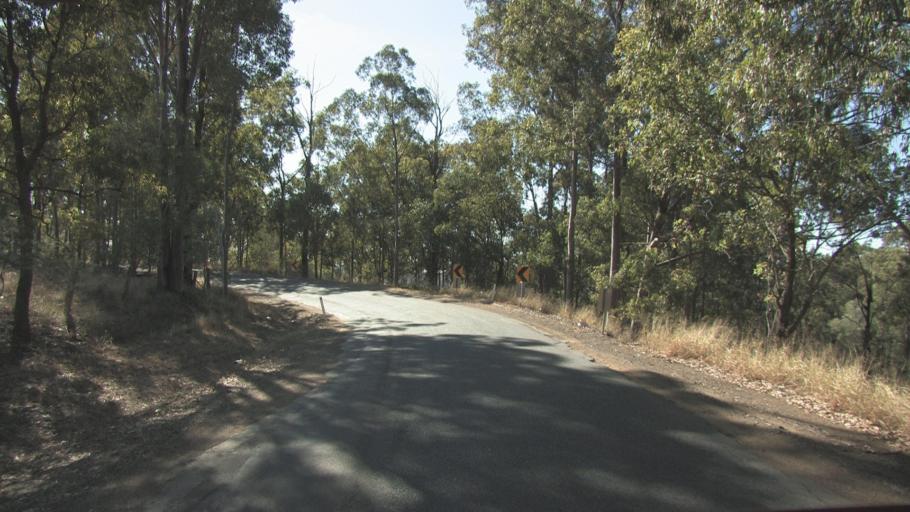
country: AU
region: Queensland
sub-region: Logan
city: Cedar Vale
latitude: -27.8927
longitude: 153.0180
